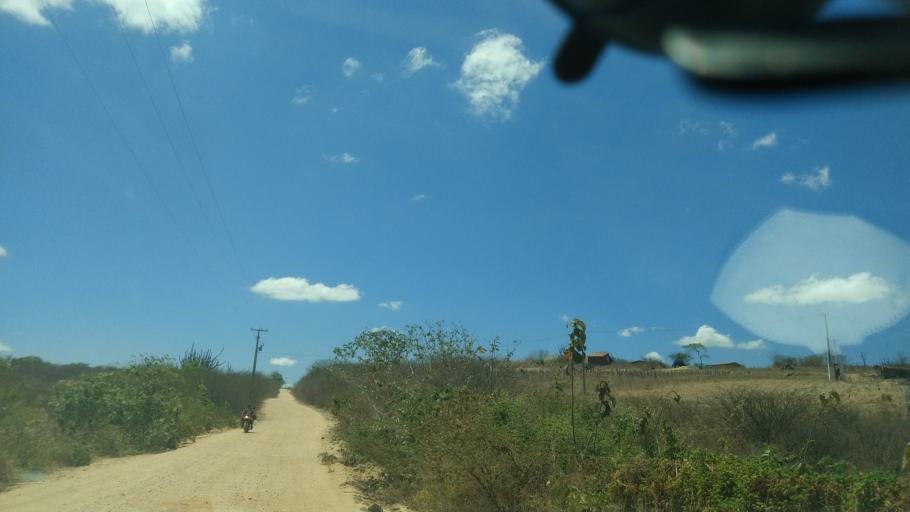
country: BR
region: Rio Grande do Norte
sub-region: Cerro Cora
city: Cerro Cora
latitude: -6.0226
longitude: -36.3327
